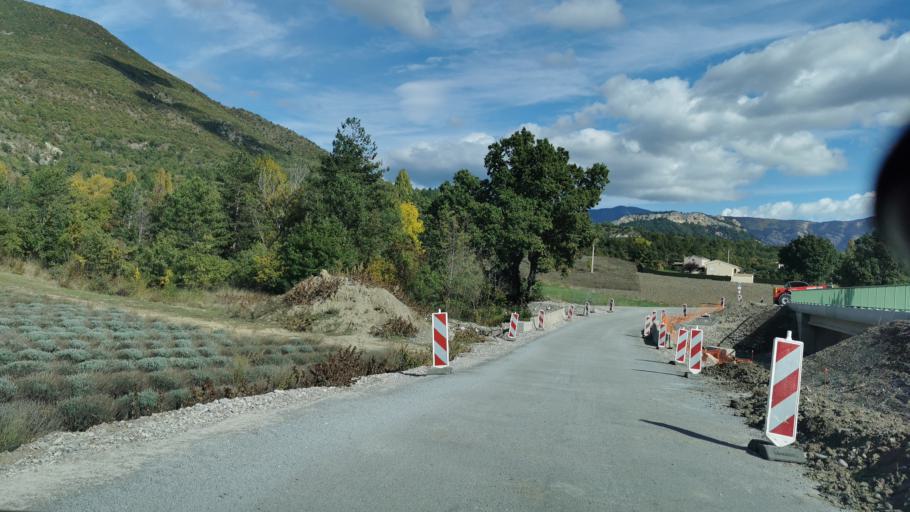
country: FR
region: Provence-Alpes-Cote d'Azur
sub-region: Departement des Alpes-de-Haute-Provence
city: Sisteron
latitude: 44.1872
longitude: 5.9935
